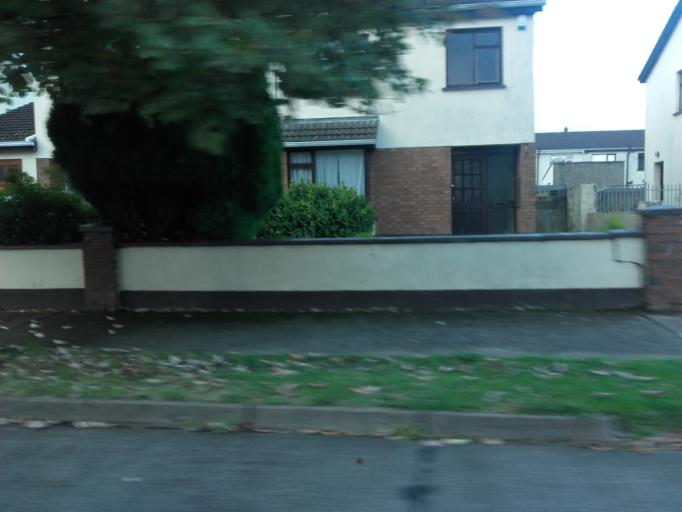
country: IE
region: Leinster
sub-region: Kildare
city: Droichead Nua
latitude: 53.1828
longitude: -6.7859
